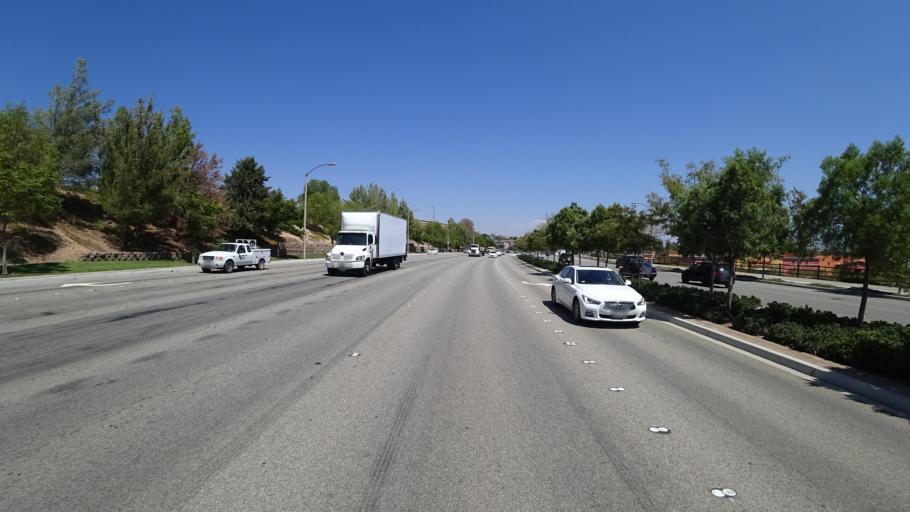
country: US
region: California
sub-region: Los Angeles County
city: Valencia
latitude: 34.4432
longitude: -118.5781
